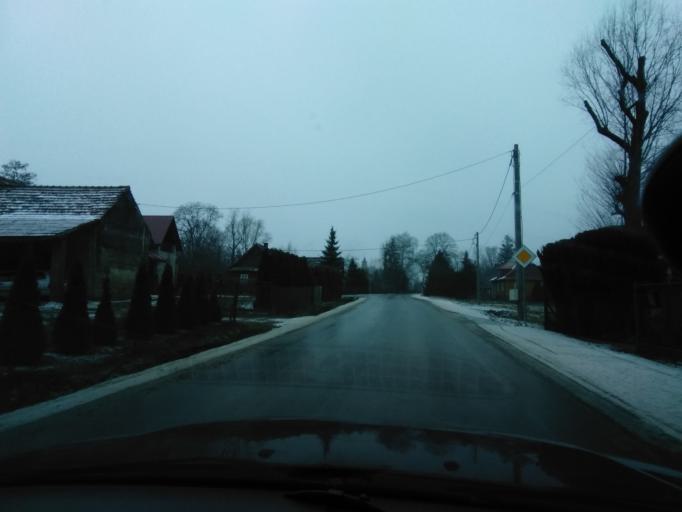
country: PL
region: Subcarpathian Voivodeship
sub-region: Powiat przeworski
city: Kanczuga
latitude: 50.0182
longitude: 22.3972
